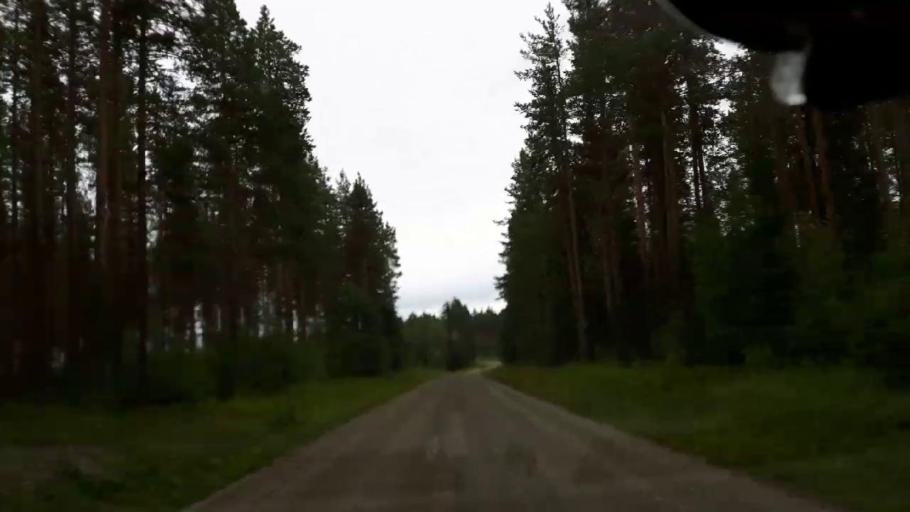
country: SE
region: Jaemtland
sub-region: Braecke Kommun
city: Braecke
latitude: 62.9451
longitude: 15.4476
